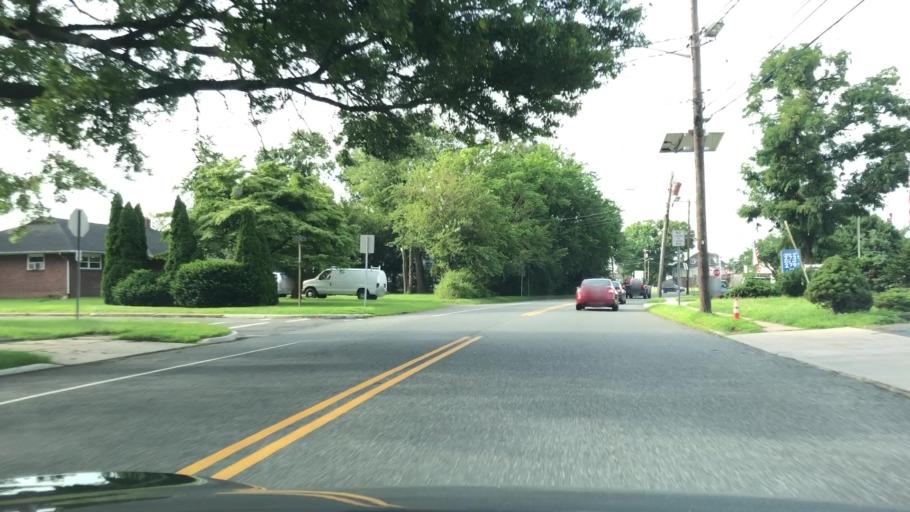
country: US
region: New Jersey
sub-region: Mercer County
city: Prospect Park
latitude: 40.2469
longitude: -74.7425
